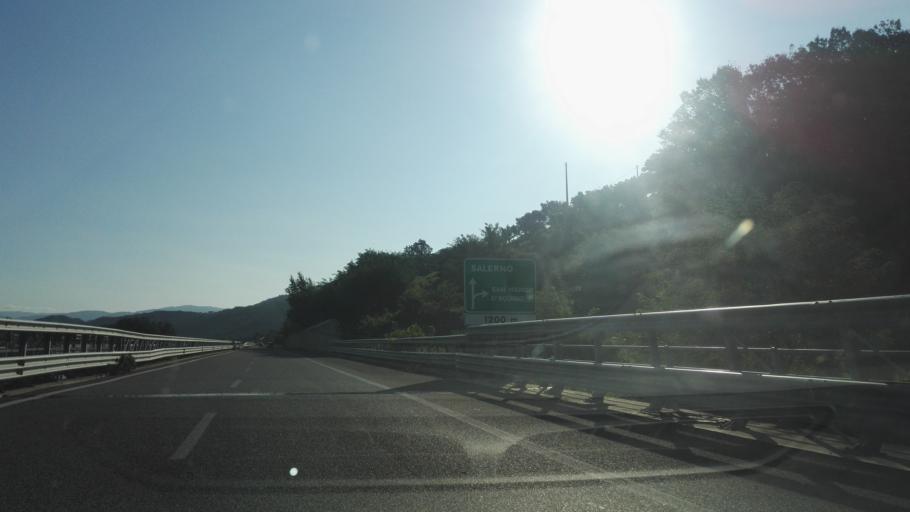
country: IT
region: Calabria
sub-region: Provincia di Catanzaro
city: Nocera Terinese
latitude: 39.0592
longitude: 16.1604
